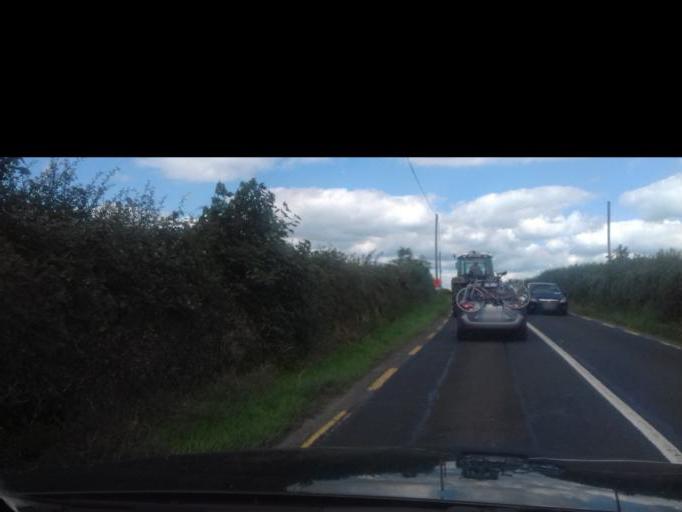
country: IE
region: Munster
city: Carrick-on-Suir
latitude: 52.2988
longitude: -7.4489
